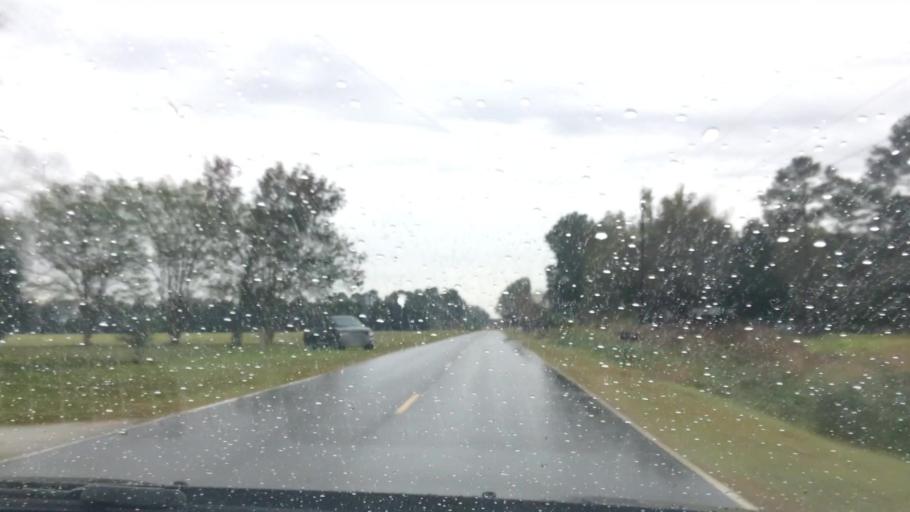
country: US
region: North Carolina
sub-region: Pitt County
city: Grifton
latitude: 35.3938
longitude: -77.3999
